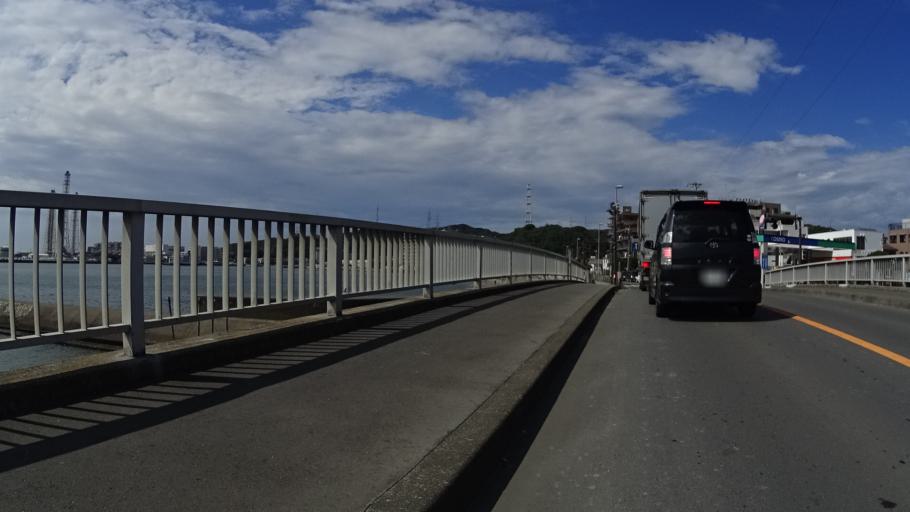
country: JP
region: Kanagawa
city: Yokosuka
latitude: 35.2269
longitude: 139.7150
